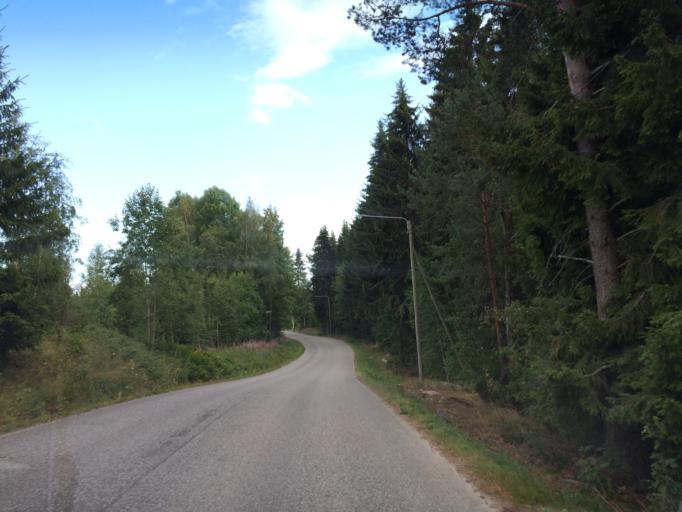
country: FI
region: Haeme
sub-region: Haemeenlinna
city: Hauho
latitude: 61.0750
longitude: 24.6657
